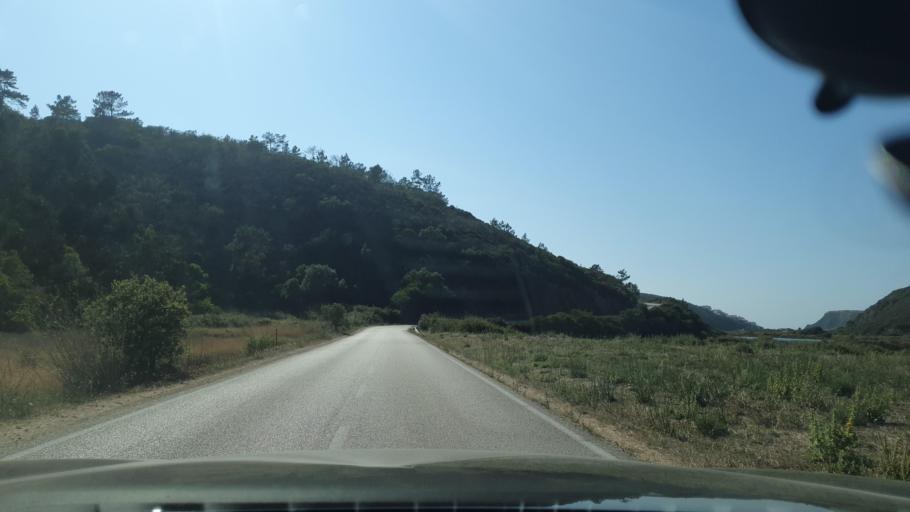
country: PT
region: Beja
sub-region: Odemira
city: Sao Teotonio
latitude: 37.4337
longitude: -8.7878
